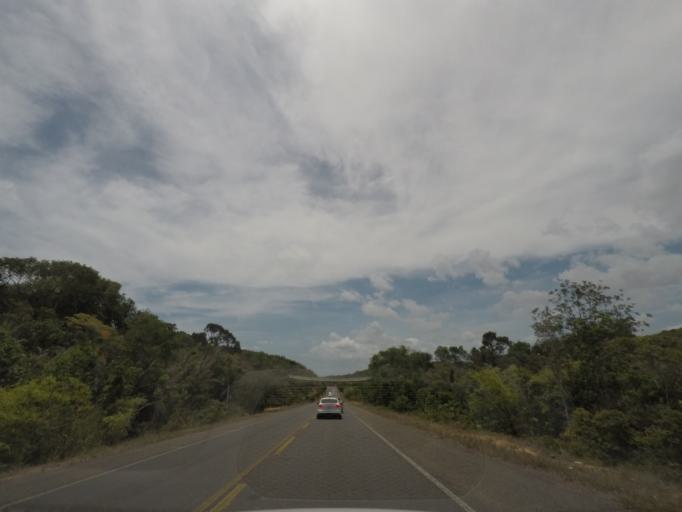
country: BR
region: Bahia
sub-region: Conde
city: Conde
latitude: -12.0231
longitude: -37.6933
